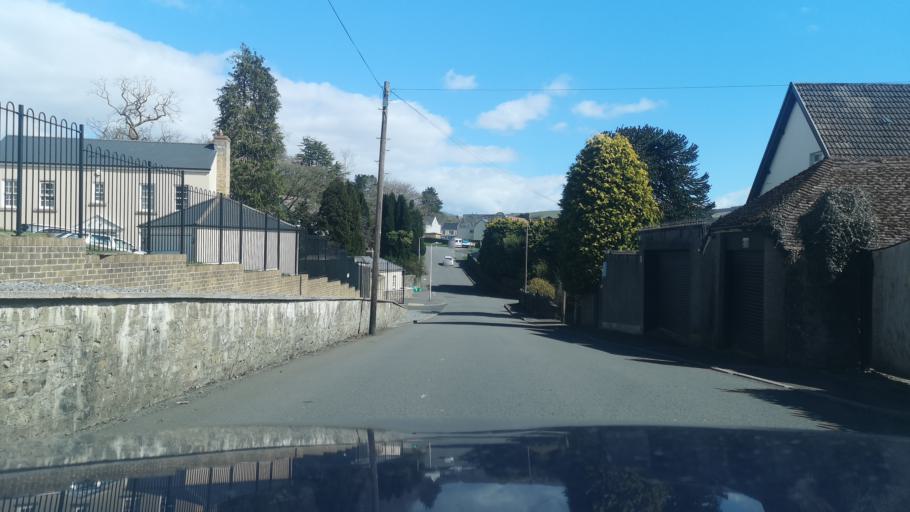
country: GB
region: Wales
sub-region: Merthyr Tydfil County Borough
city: Merthyr Tydfil
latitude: 51.7551
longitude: -3.3807
